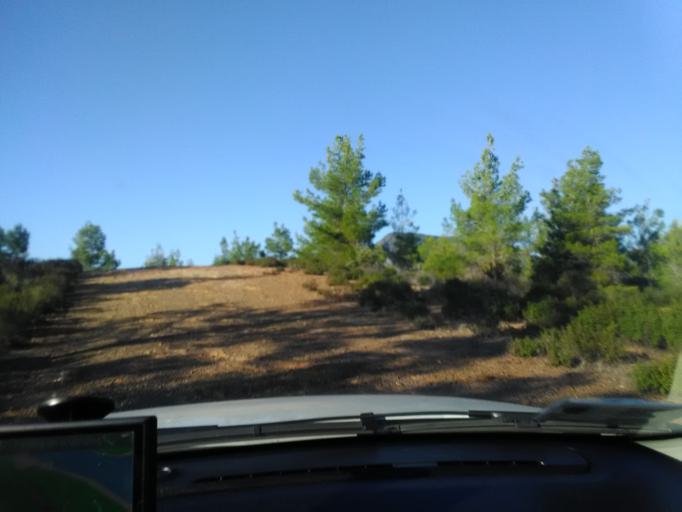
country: TR
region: Antalya
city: Gazipasa
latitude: 36.3073
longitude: 32.3977
